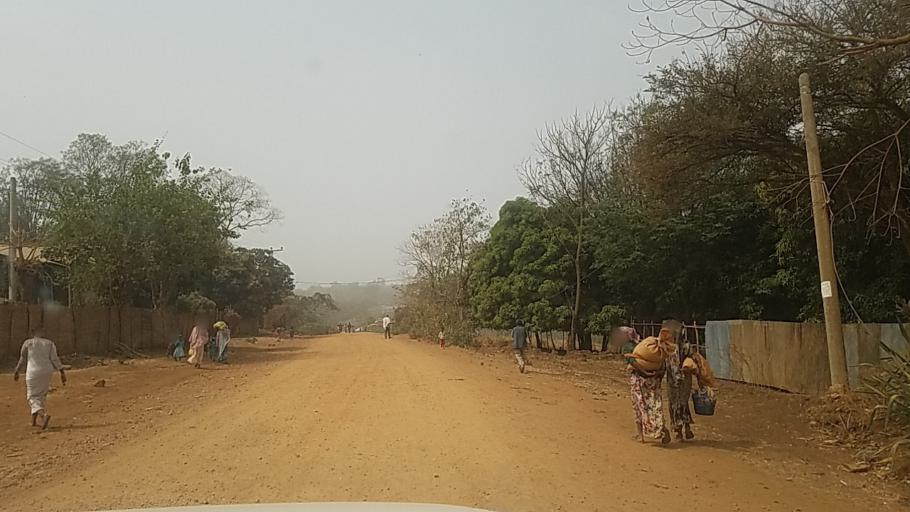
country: ET
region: Amhara
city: Bure
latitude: 10.7773
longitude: 36.2684
